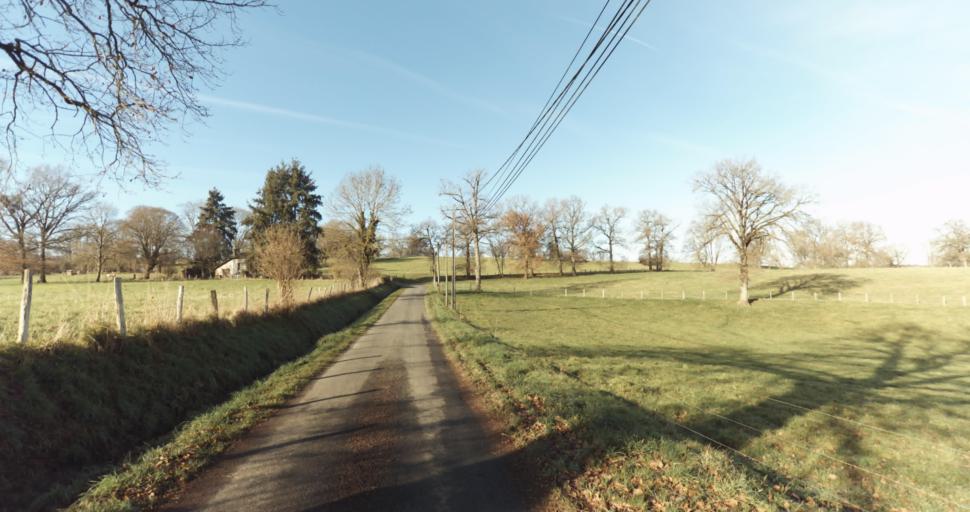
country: FR
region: Limousin
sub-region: Departement de la Haute-Vienne
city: Saint-Priest-sous-Aixe
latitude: 45.7932
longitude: 1.1088
